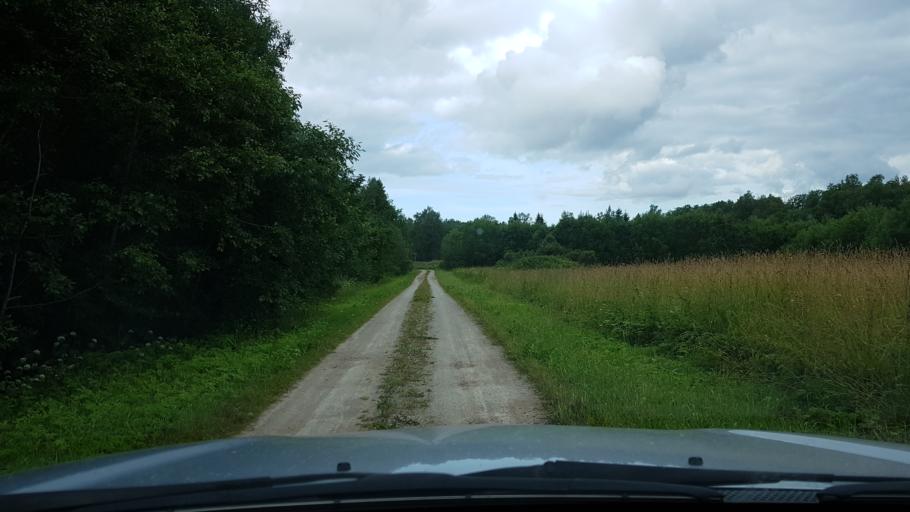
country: EE
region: Ida-Virumaa
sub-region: Narva-Joesuu linn
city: Narva-Joesuu
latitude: 59.4038
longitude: 27.9626
